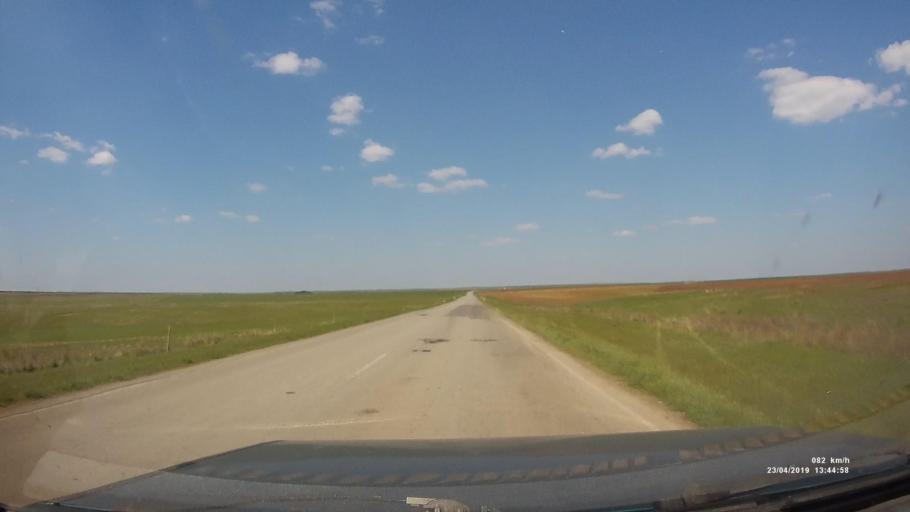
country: RU
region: Kalmykiya
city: Yashalta
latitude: 46.5871
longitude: 42.8193
